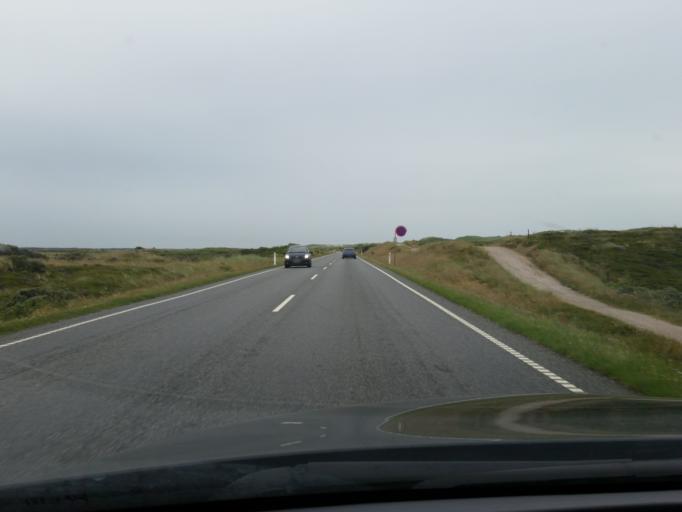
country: DK
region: Central Jutland
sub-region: Ringkobing-Skjern Kommune
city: Hvide Sande
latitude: 55.8314
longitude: 8.1727
